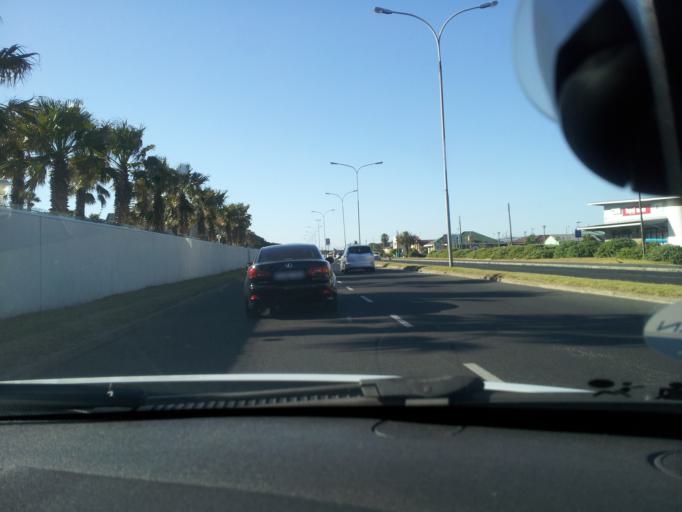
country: ZA
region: Western Cape
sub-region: Overberg District Municipality
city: Grabouw
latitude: -34.1326
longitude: 18.8445
